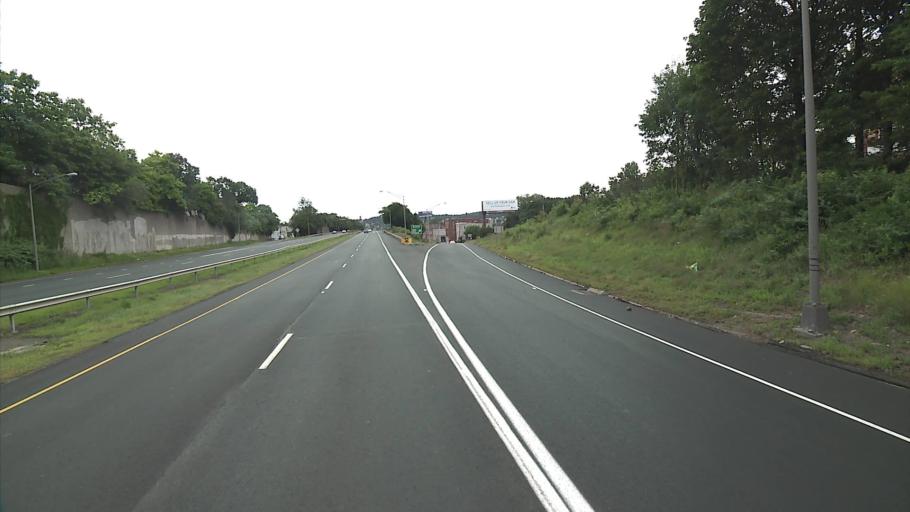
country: US
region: Connecticut
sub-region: New Haven County
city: Waterbury
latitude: 41.5379
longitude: -73.0440
